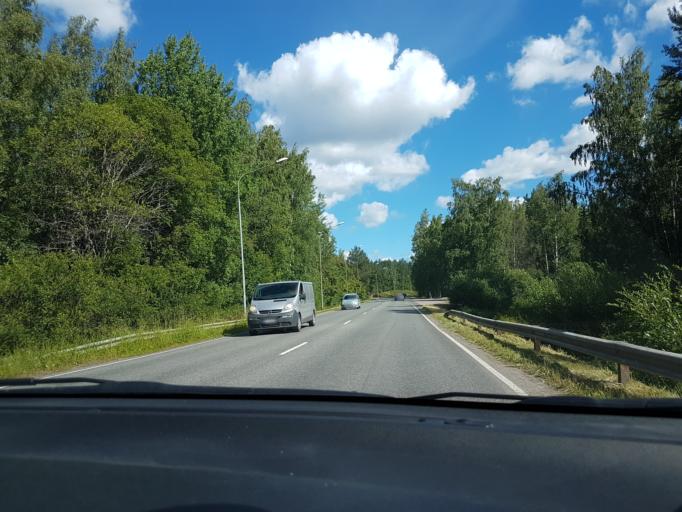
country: FI
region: Uusimaa
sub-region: Helsinki
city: Kerava
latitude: 60.3846
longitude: 25.0983
